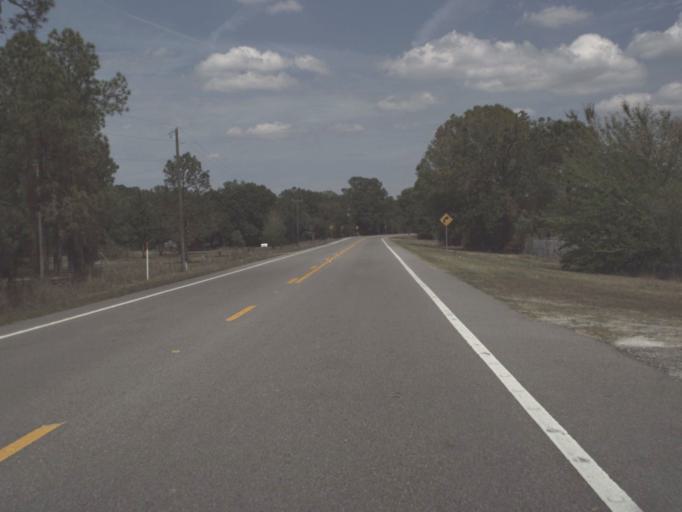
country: US
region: Florida
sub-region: Hernando County
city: Ridge Manor
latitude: 28.5451
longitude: -82.0909
